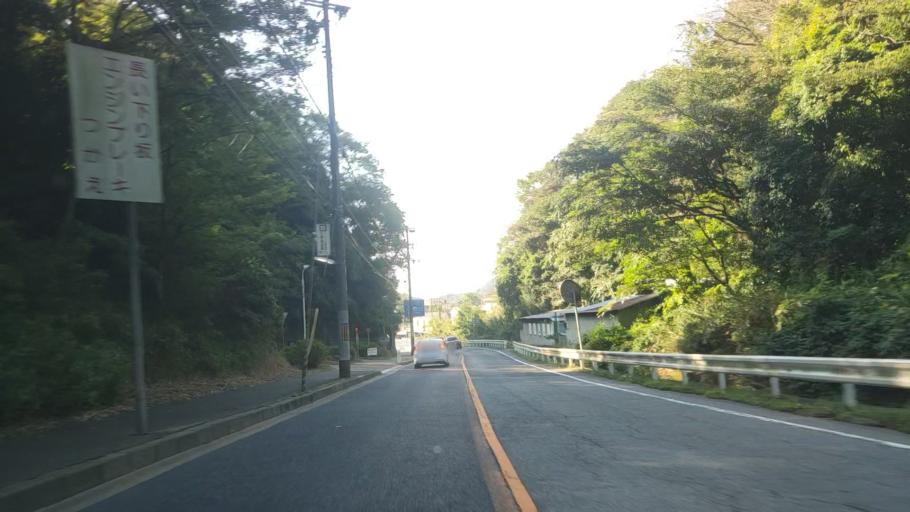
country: JP
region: Hyogo
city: Kobe
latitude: 34.7323
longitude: 135.1593
